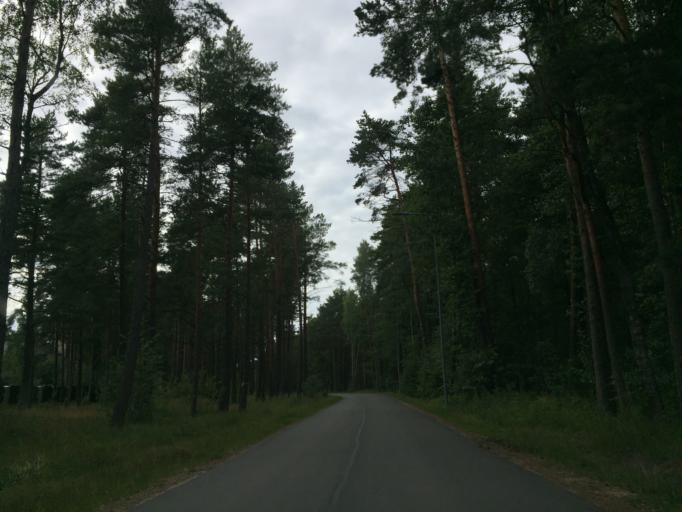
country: LV
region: Carnikava
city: Carnikava
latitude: 57.1337
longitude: 24.2512
